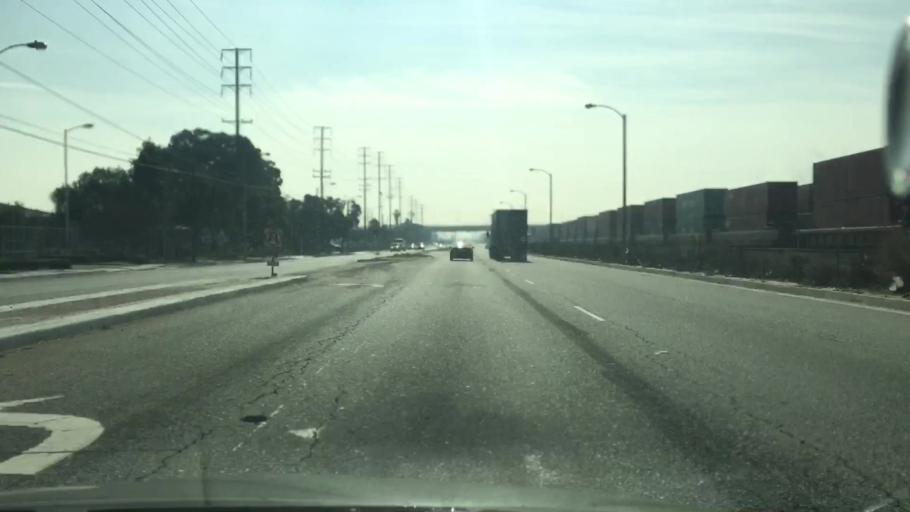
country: US
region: California
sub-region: Los Angeles County
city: Carson
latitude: 33.8129
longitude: -118.2329
